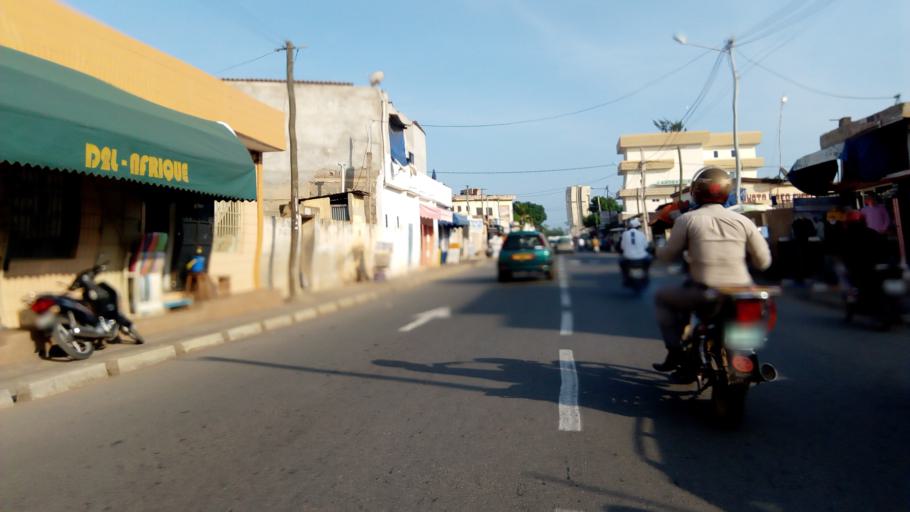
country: TG
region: Maritime
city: Lome
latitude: 6.1349
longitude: 1.2113
